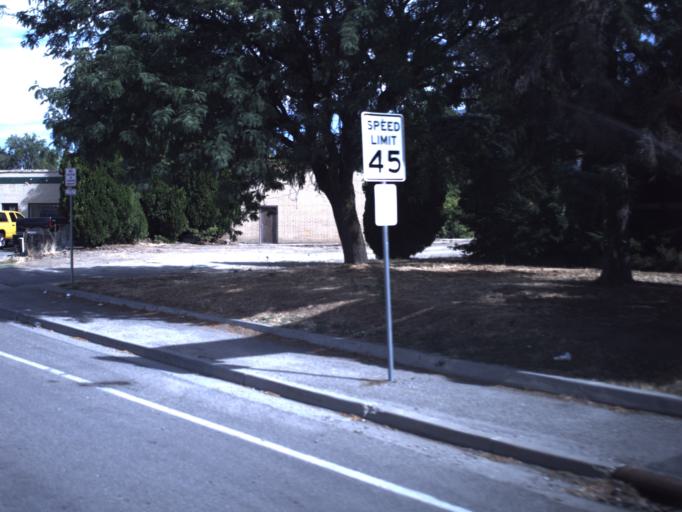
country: US
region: Utah
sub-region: Weber County
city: Harrisville
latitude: 41.2720
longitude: -111.9784
